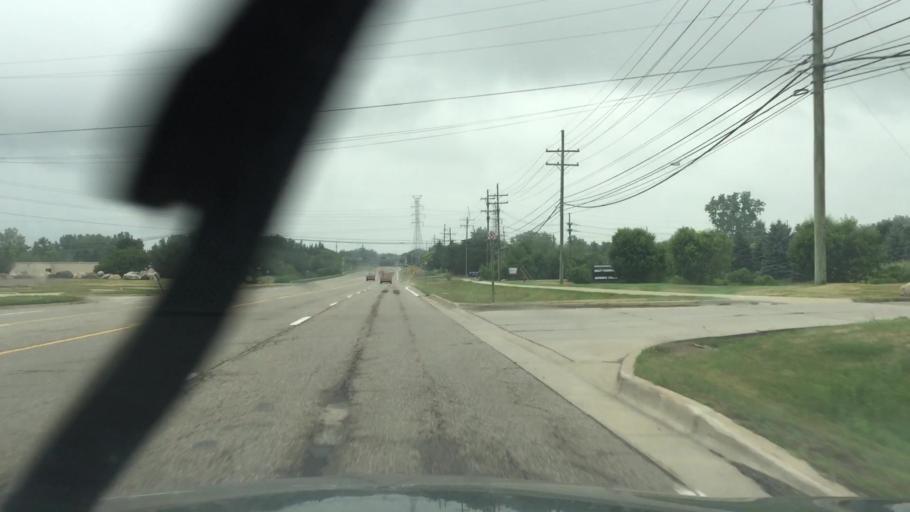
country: US
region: Michigan
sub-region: Oakland County
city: Wixom
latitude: 42.5124
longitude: -83.5369
